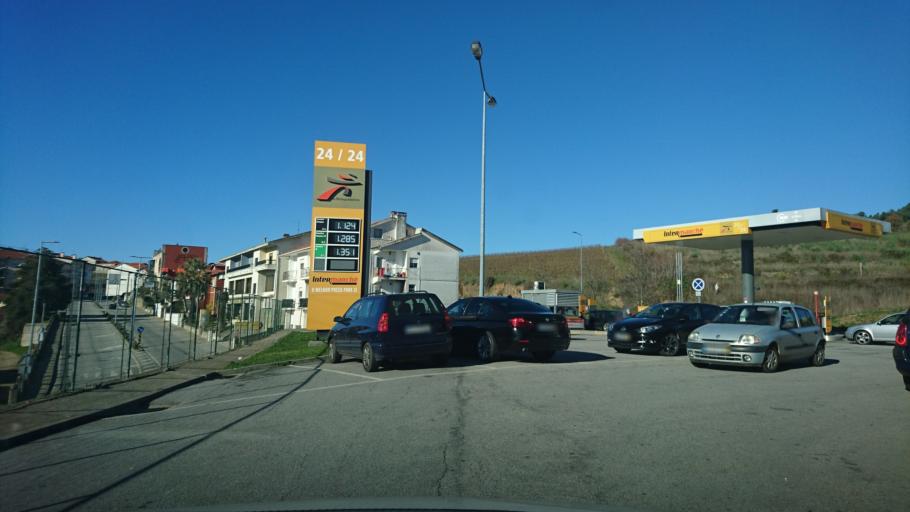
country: PT
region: Braganca
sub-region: Braganca Municipality
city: Vila Flor
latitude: 41.3099
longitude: -7.1629
